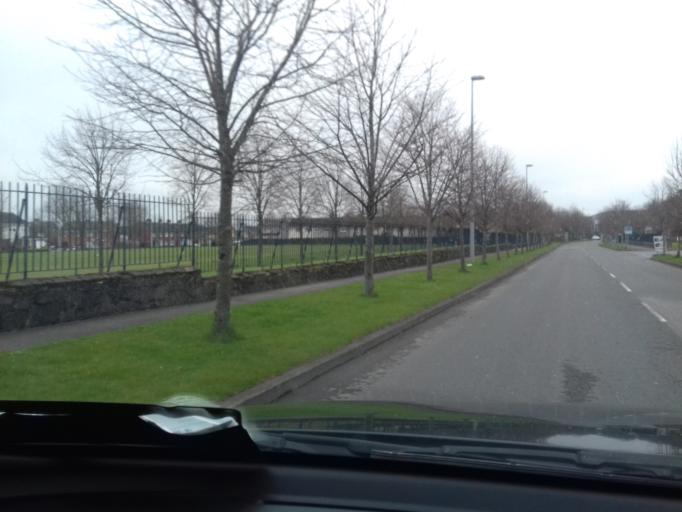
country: IE
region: Leinster
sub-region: Dublin City
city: Finglas
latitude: 53.4004
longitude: -6.3129
